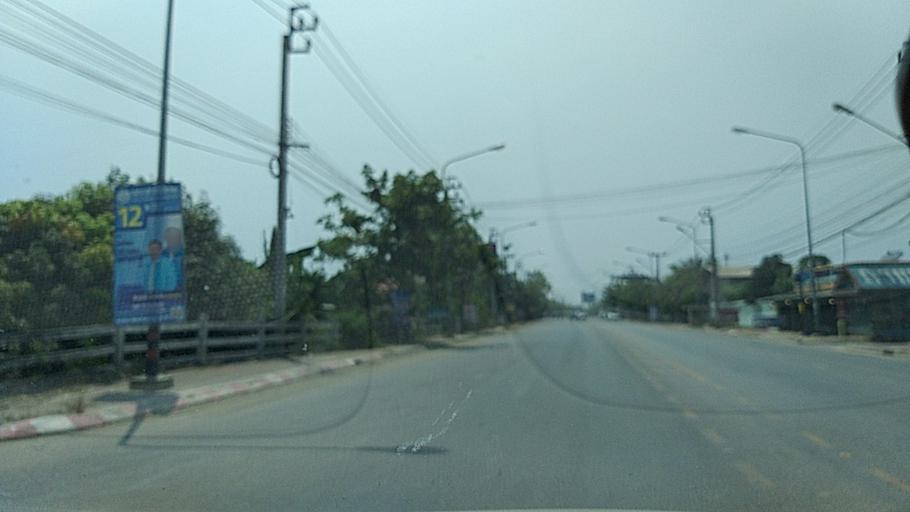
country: TH
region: Nonthaburi
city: Bang Yai
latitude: 13.9100
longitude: 100.3369
